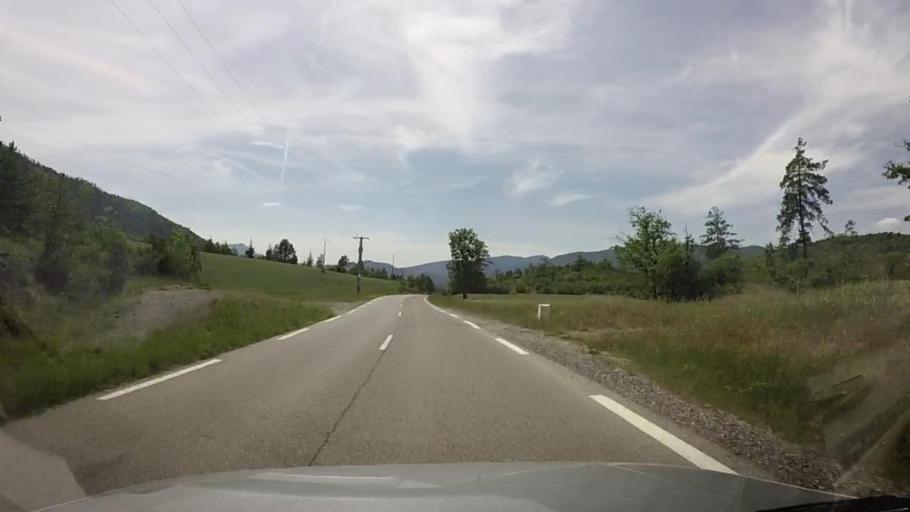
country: FR
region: Provence-Alpes-Cote d'Azur
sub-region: Departement des Alpes-de-Haute-Provence
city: Le Brusquet
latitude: 44.1653
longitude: 6.3231
